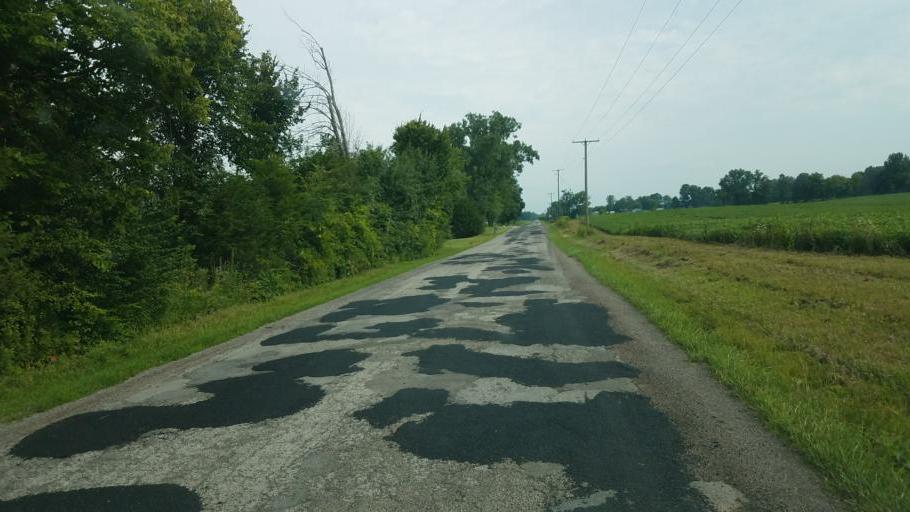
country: US
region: Ohio
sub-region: Morrow County
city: Cardington
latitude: 40.4756
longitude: -82.9036
